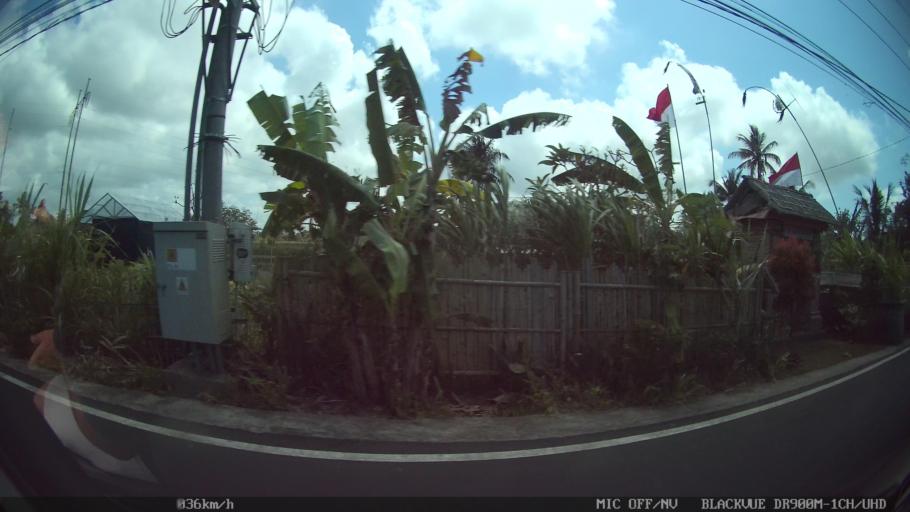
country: ID
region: Bali
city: Banjar Pasekan
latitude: -8.5995
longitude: 115.3034
